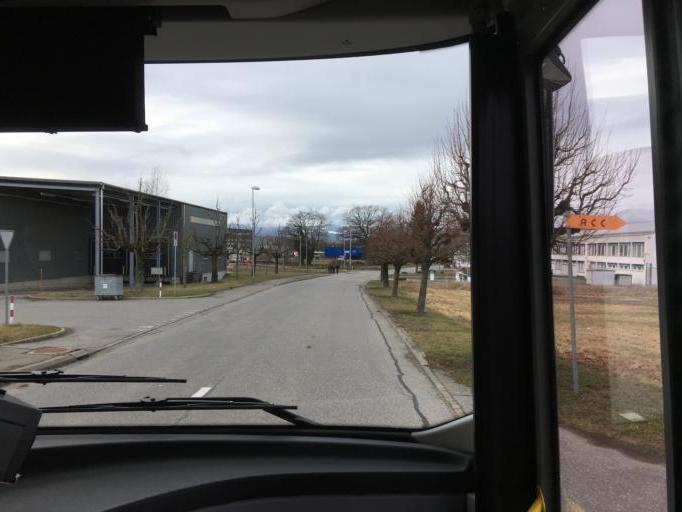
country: CH
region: Vaud
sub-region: Broye-Vully District
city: Avenches
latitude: 46.8864
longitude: 7.0464
